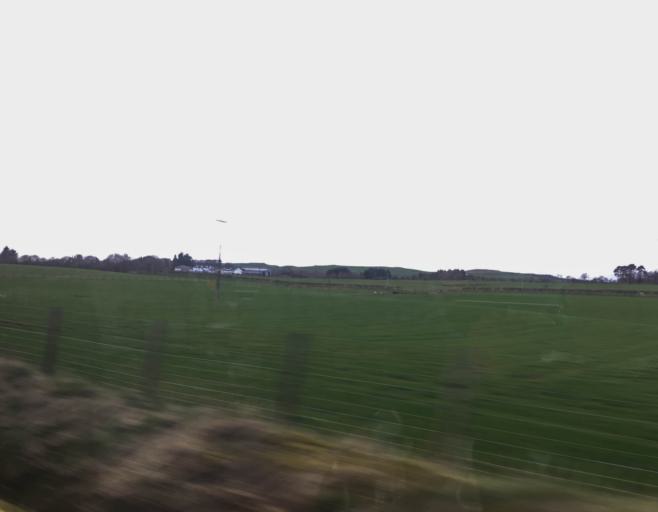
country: GB
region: Scotland
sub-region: Dumfries and Galloway
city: Annan
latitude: 55.0667
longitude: -3.2711
